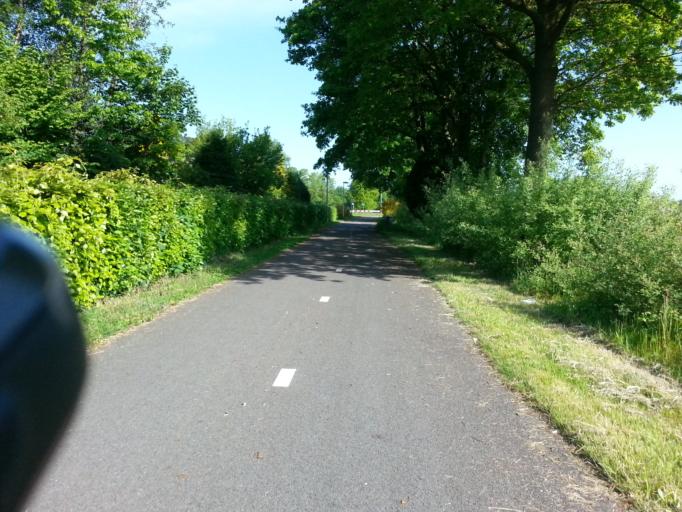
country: NL
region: Gelderland
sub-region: Berkelland
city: Eibergen
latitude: 52.1179
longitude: 6.6337
